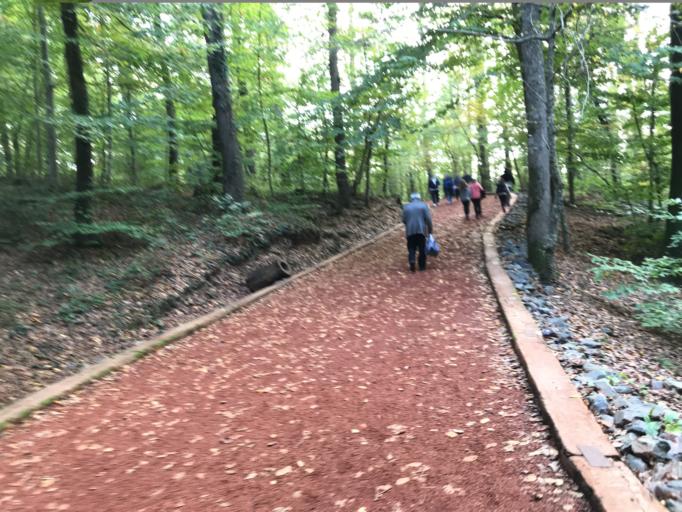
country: TR
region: Istanbul
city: Kemerburgaz
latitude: 41.1780
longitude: 28.9598
